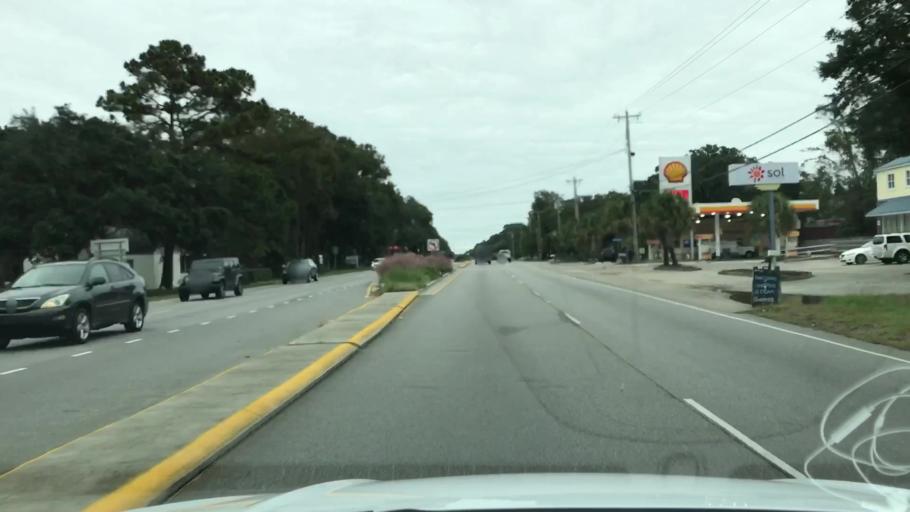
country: US
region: South Carolina
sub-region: Georgetown County
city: Murrells Inlet
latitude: 33.4577
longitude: -79.1140
